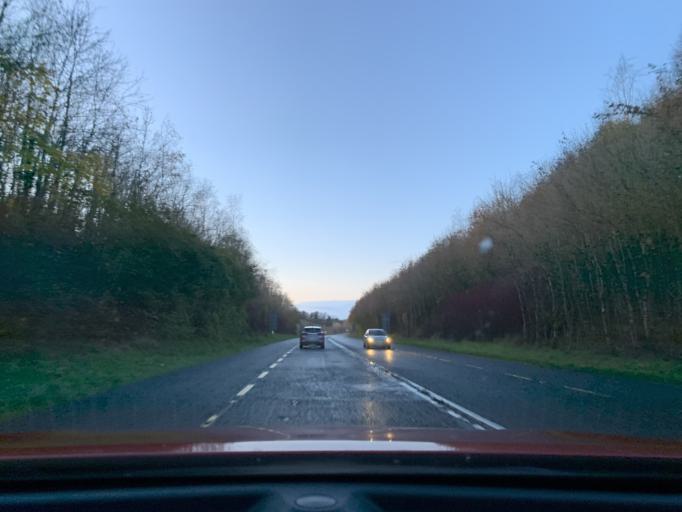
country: IE
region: Connaught
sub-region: County Leitrim
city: Carrick-on-Shannon
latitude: 53.9216
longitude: -7.9902
